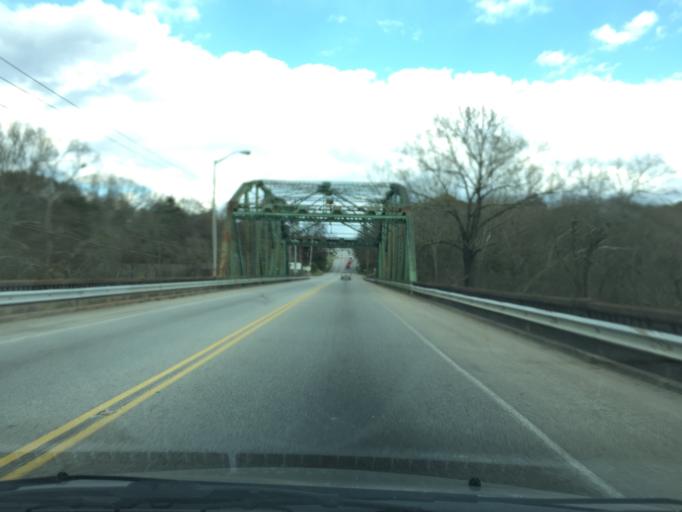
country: US
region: Tennessee
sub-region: Hamilton County
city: East Chattanooga
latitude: 35.0801
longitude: -85.2192
